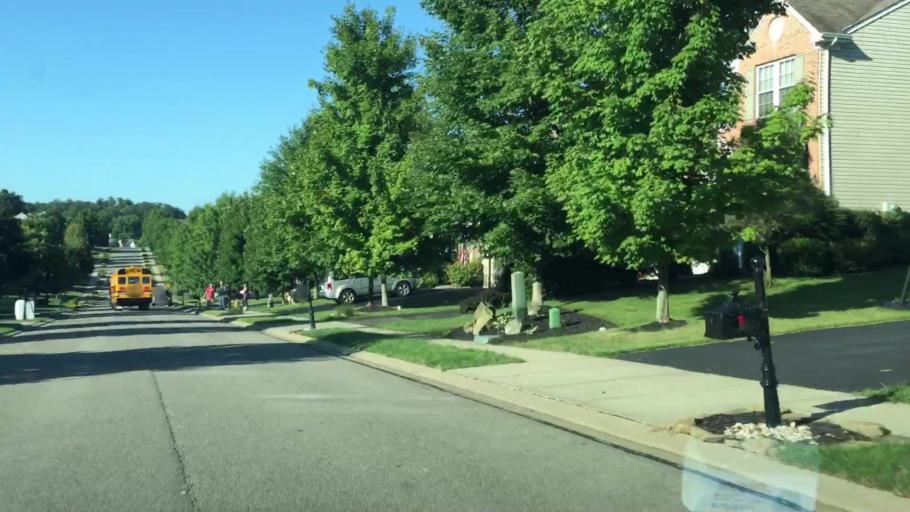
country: US
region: Pennsylvania
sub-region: Allegheny County
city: Franklin Park
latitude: 40.5933
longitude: -80.0942
